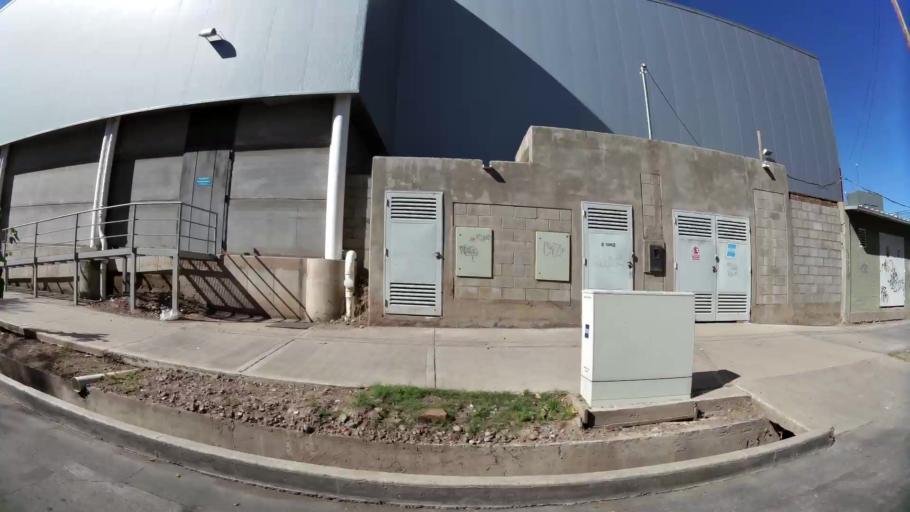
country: AR
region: Mendoza
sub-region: Departamento de Godoy Cruz
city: Godoy Cruz
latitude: -32.9256
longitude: -68.8360
